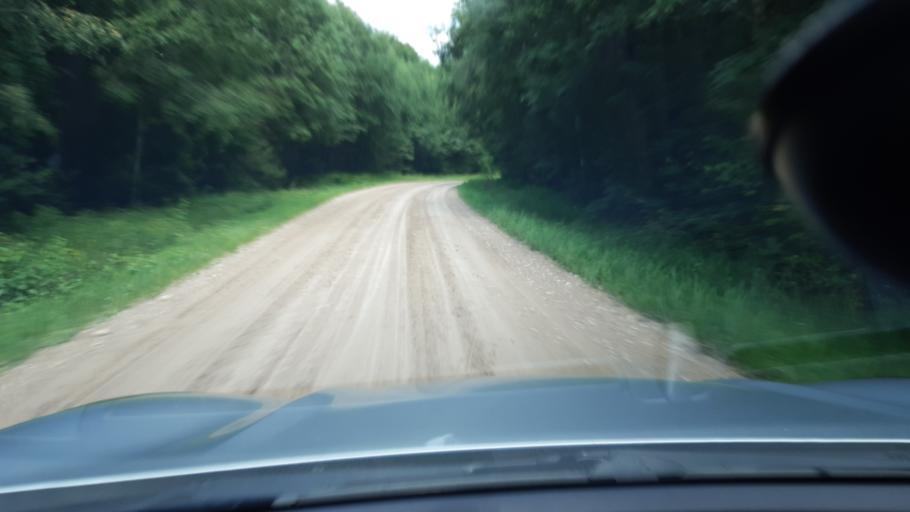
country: EE
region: Jaervamaa
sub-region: Tueri vald
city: Tueri
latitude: 58.9266
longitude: 25.2155
